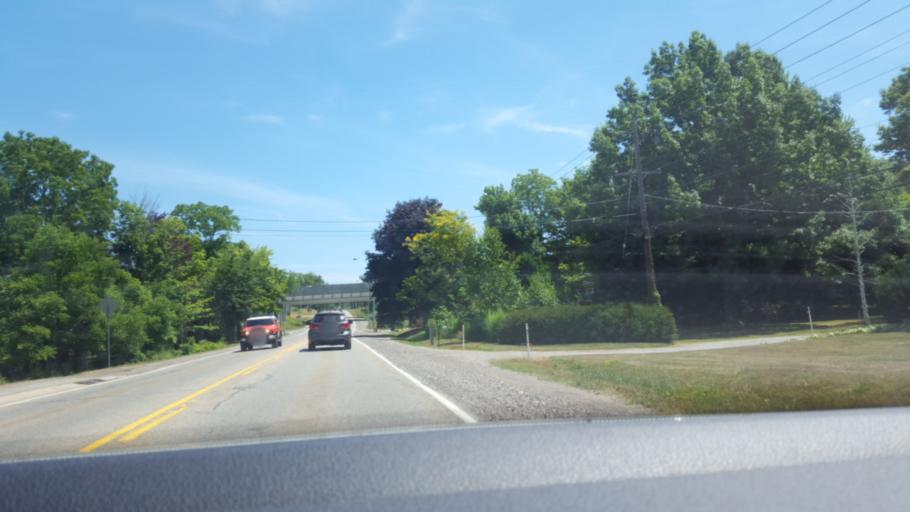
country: CA
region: Ontario
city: Ancaster
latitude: 43.2039
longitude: -79.9688
